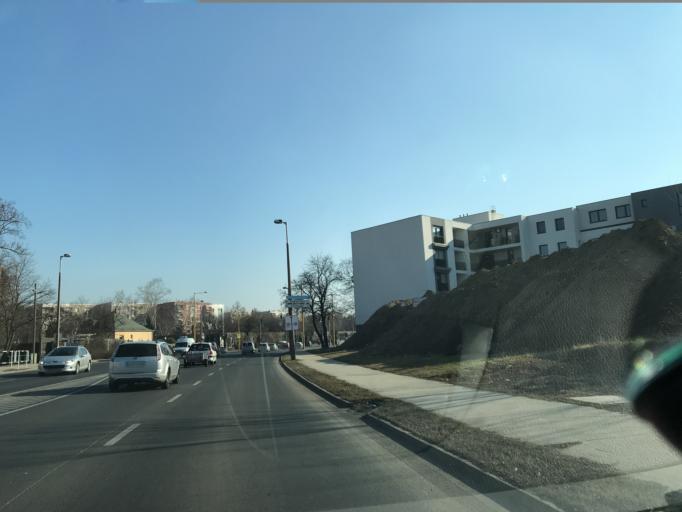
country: HU
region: Gyor-Moson-Sopron
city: Gyor
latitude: 47.6745
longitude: 17.6317
